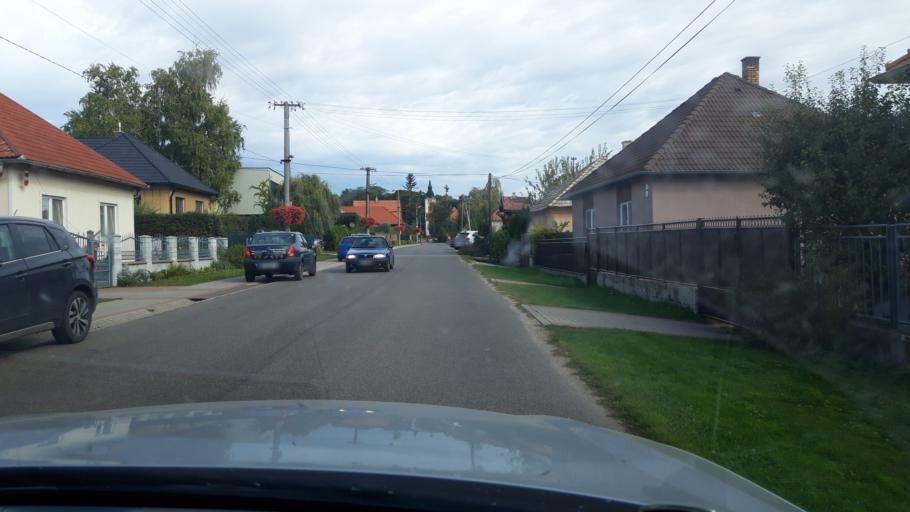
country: SK
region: Nitriansky
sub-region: Okres Nitra
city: Vrable
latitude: 48.1388
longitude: 18.3386
